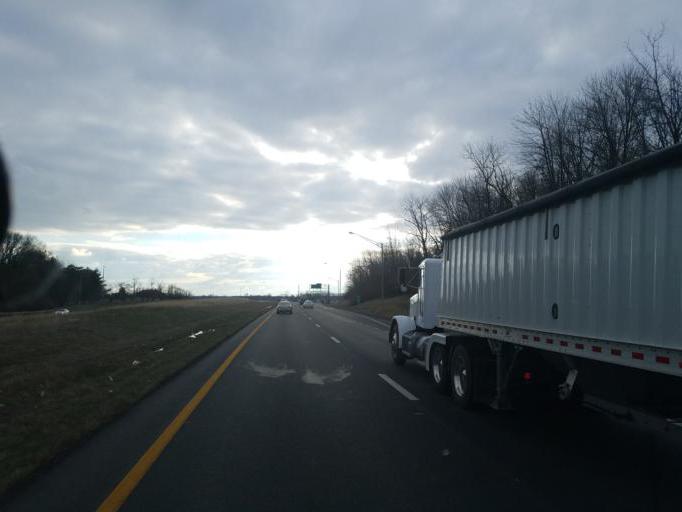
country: US
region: Missouri
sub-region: Saint Louis County
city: Glasgow Village
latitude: 38.7676
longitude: -90.1891
